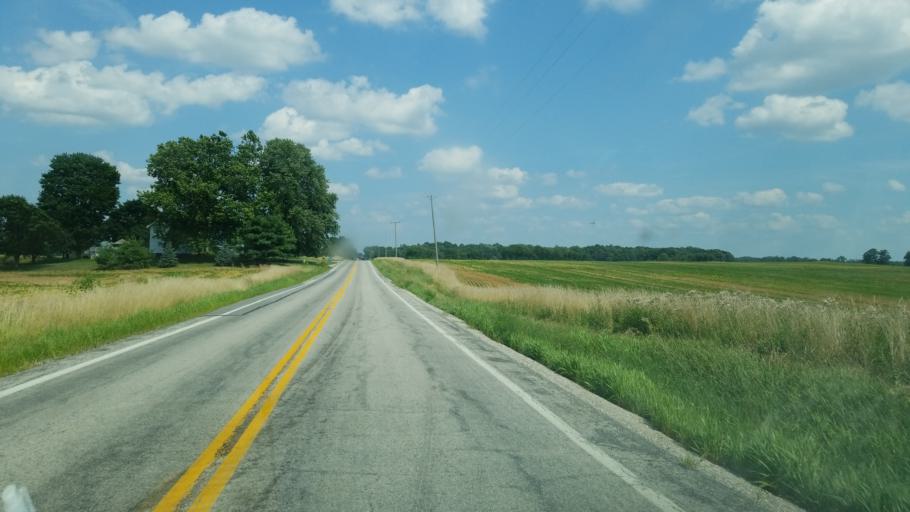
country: US
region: Ohio
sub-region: Huron County
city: Willard
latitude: 41.1045
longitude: -82.6515
